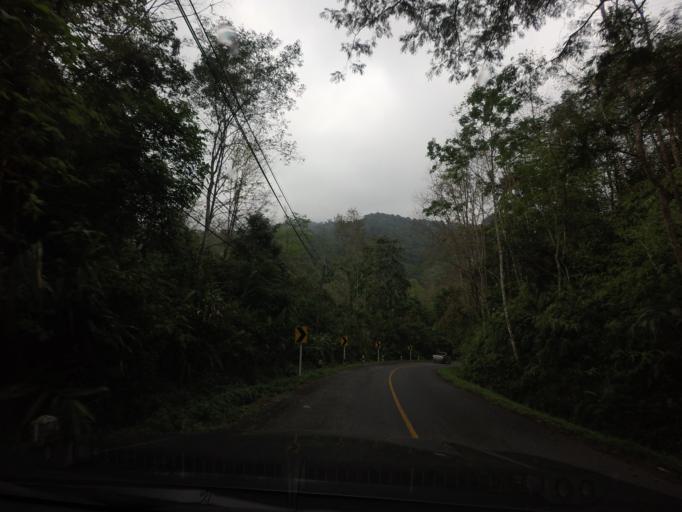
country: TH
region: Nan
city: Bo Kluea
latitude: 19.1980
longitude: 101.0812
